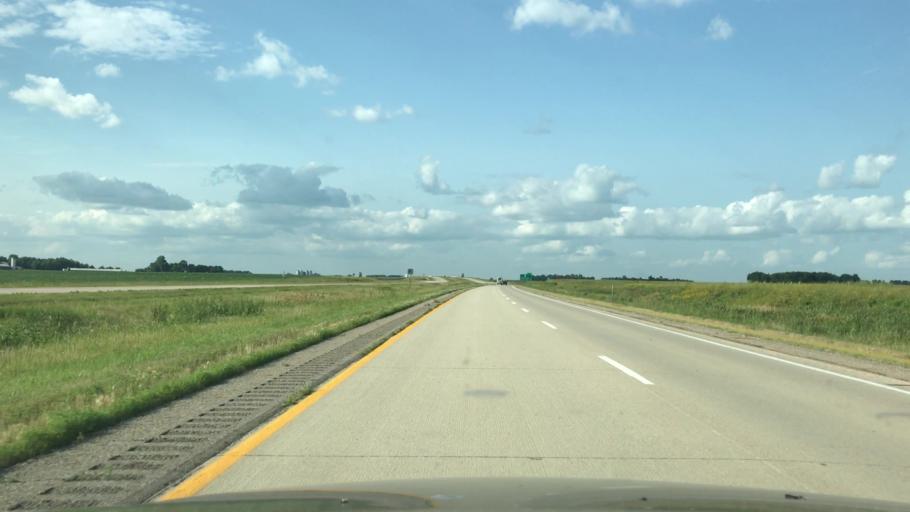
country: US
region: Iowa
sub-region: Osceola County
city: Sibley
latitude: 43.4232
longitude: -95.7157
